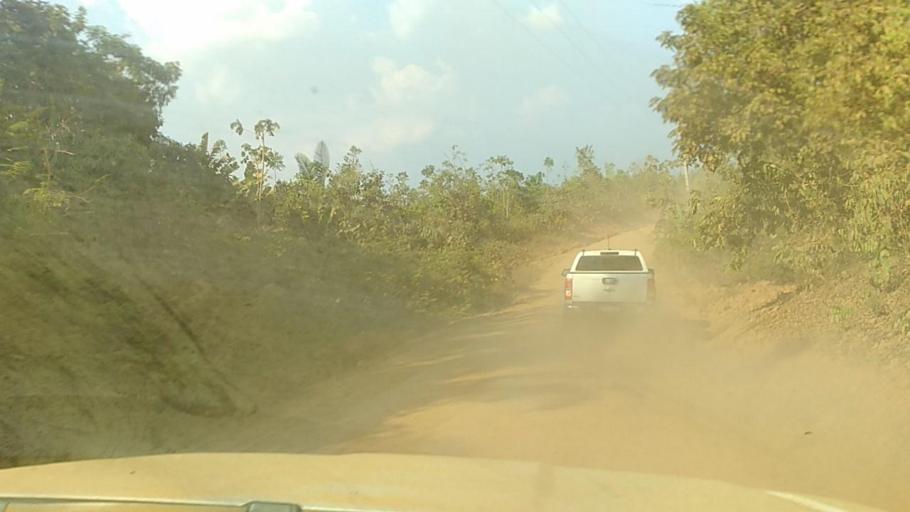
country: BR
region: Rondonia
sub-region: Porto Velho
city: Porto Velho
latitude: -8.6710
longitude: -64.0004
